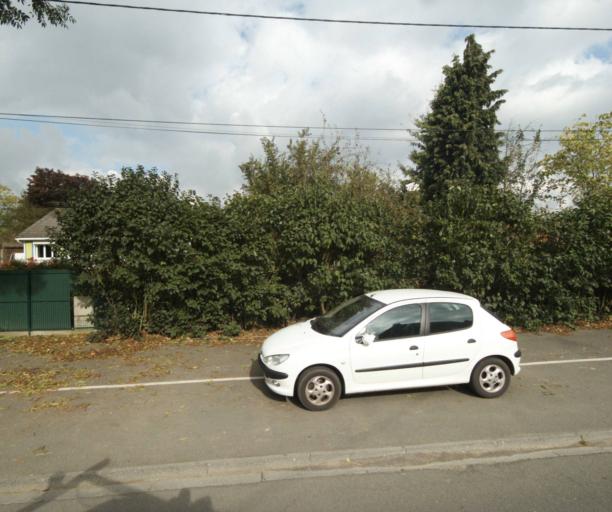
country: FR
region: Nord-Pas-de-Calais
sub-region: Departement du Nord
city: Fournes-en-Weppes
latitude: 50.5833
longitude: 2.8829
